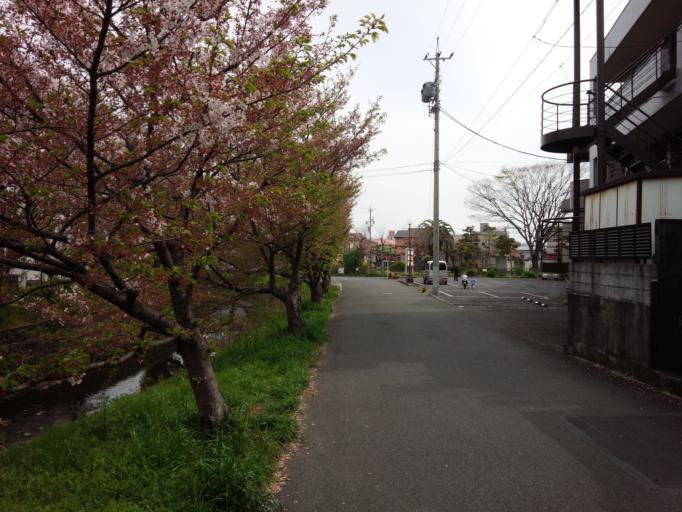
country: JP
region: Shizuoka
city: Shizuoka-shi
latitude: 35.0096
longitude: 138.4707
